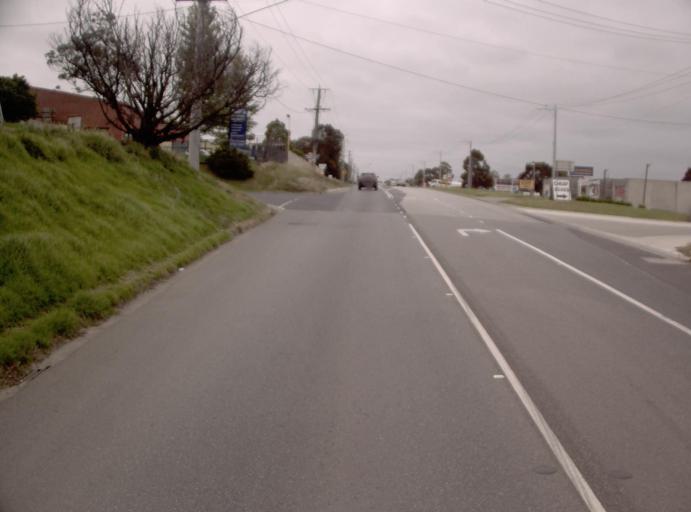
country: AU
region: Victoria
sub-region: Casey
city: Hallam
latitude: -38.0139
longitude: 145.2717
